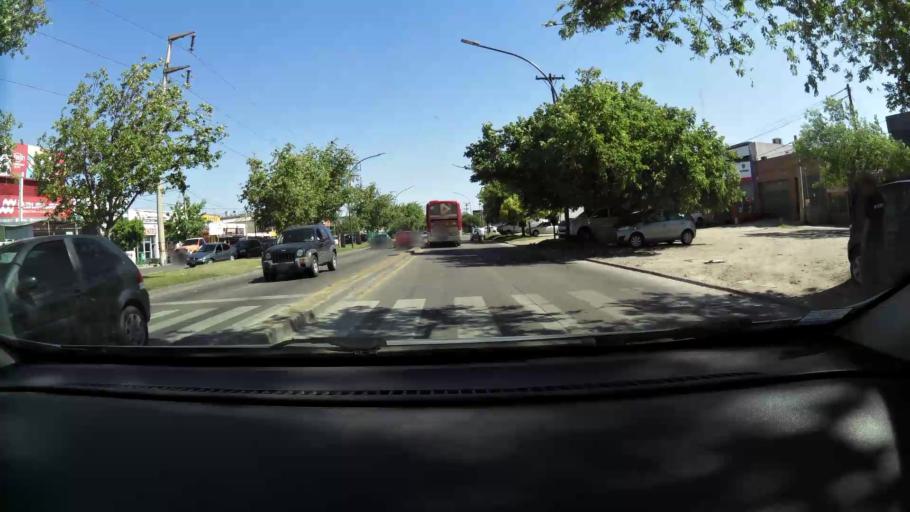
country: AR
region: Cordoba
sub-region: Departamento de Capital
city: Cordoba
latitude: -31.3768
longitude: -64.1761
